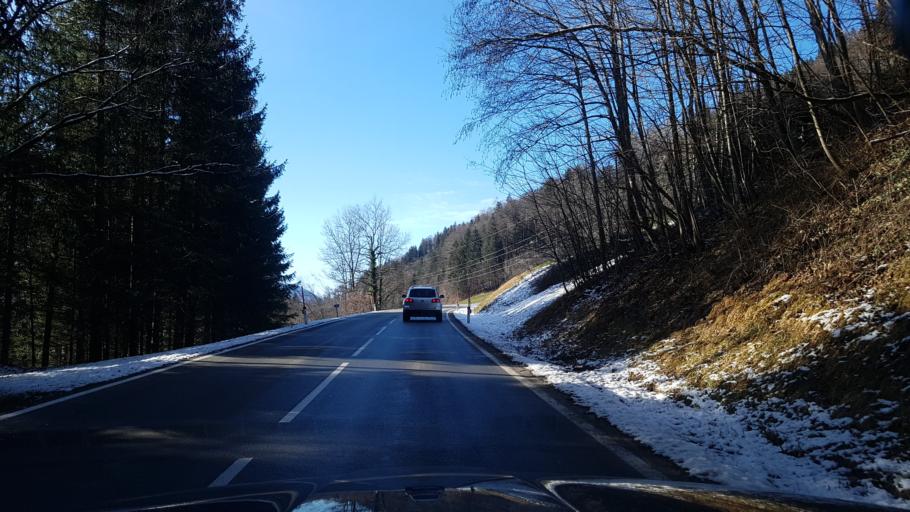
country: AT
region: Salzburg
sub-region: Politischer Bezirk Salzburg-Umgebung
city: Koppl
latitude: 47.7782
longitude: 13.1215
